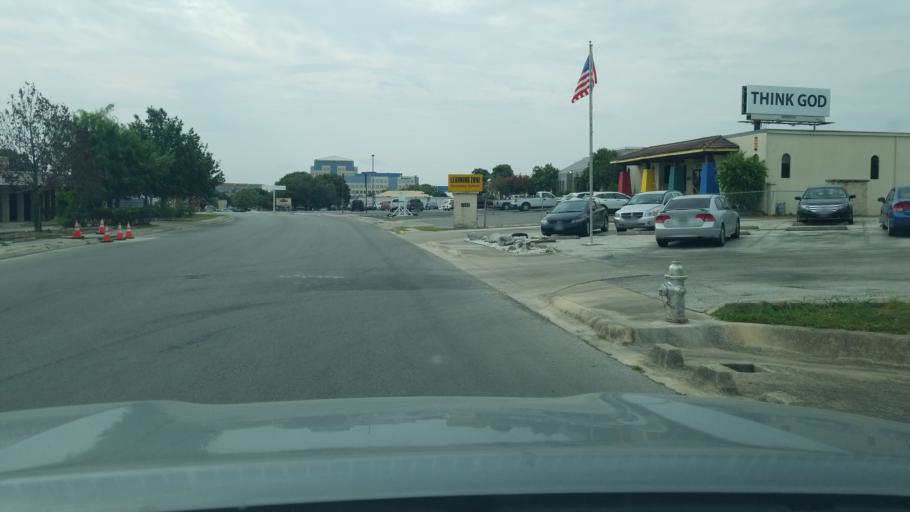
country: US
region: Texas
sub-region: Bexar County
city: Castle Hills
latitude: 29.5364
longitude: -98.4896
